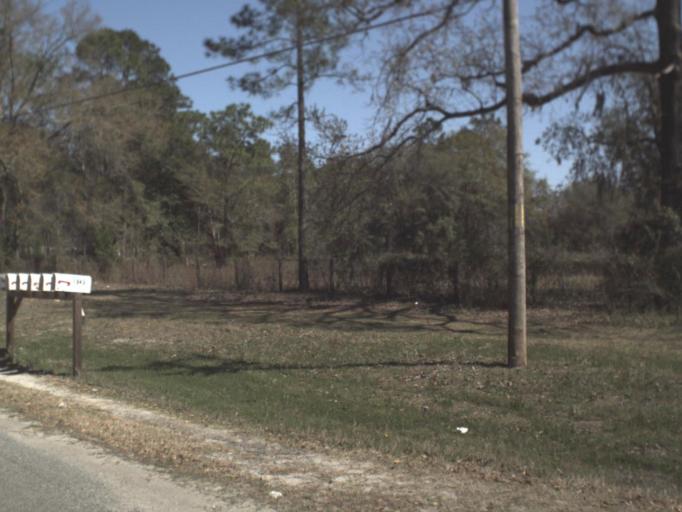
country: US
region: Florida
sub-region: Leon County
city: Woodville
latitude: 30.3256
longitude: -84.3114
